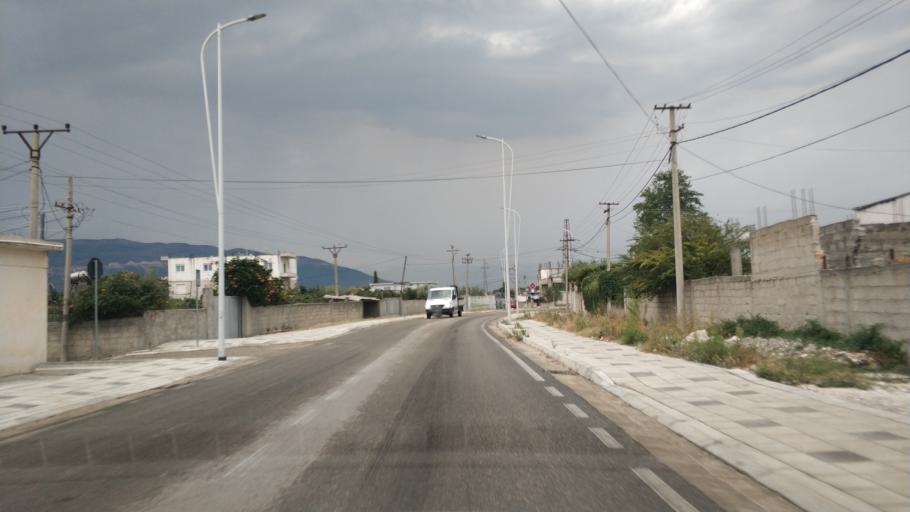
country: AL
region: Vlore
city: Vlore
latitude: 40.4771
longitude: 19.4673
